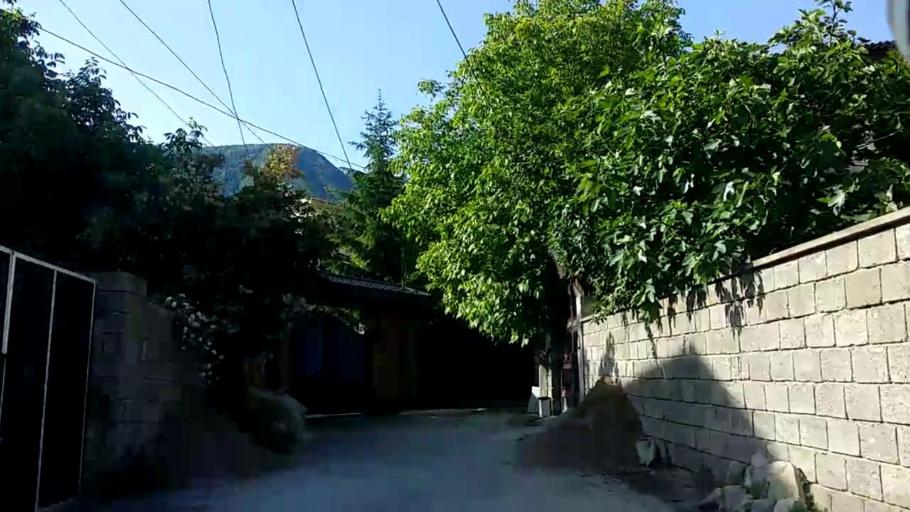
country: IR
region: Mazandaran
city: `Abbasabad
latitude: 36.5022
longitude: 51.1568
